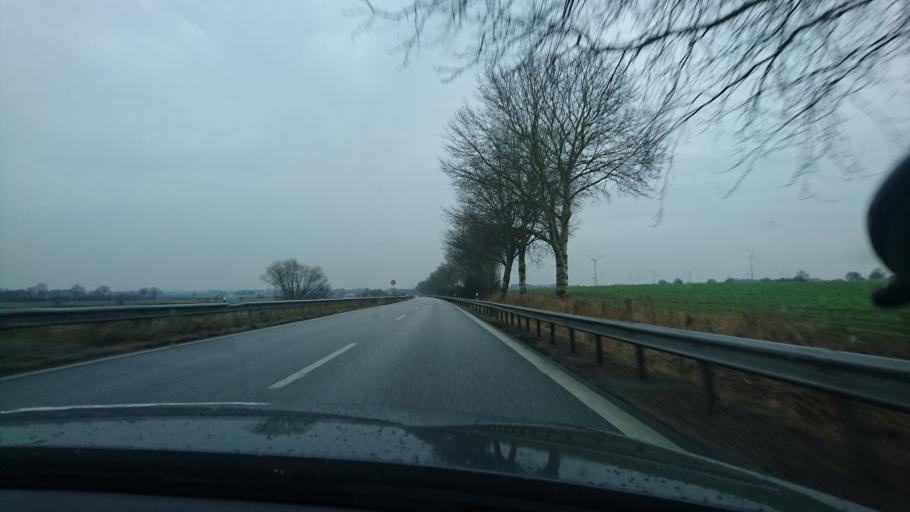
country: DE
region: Schleswig-Holstein
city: Altenkrempe
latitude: 54.1374
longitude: 10.8404
